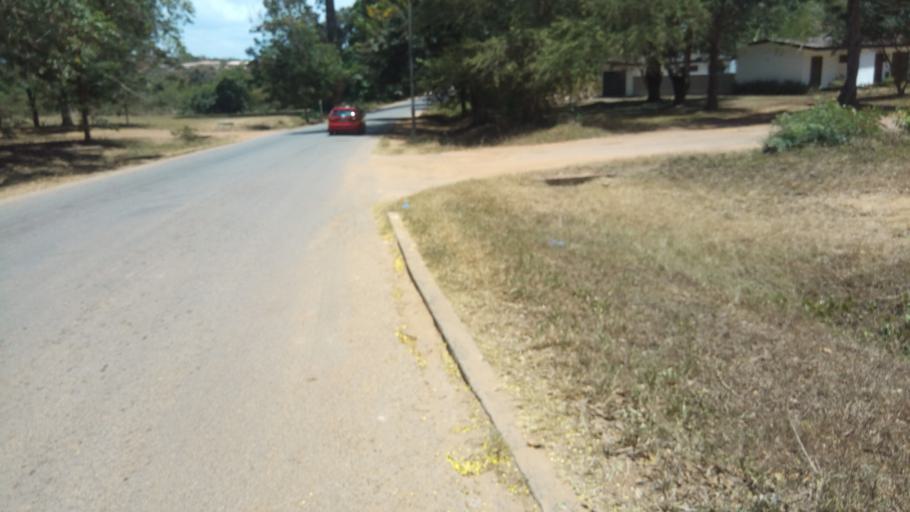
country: GH
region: Central
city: Cape Coast
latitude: 5.1280
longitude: -1.2917
